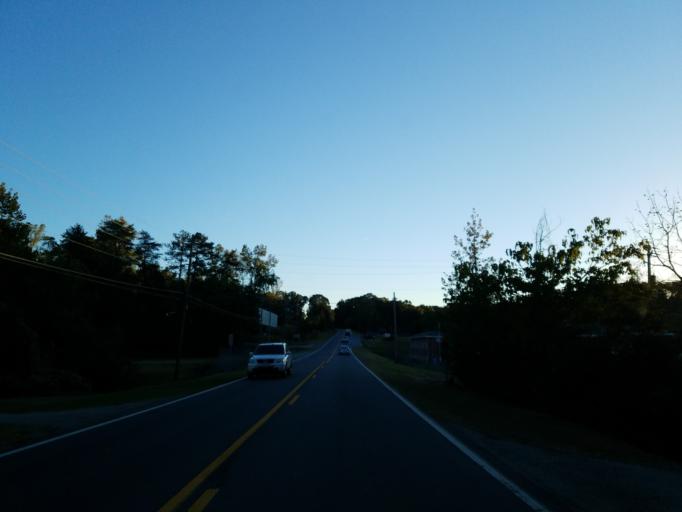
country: US
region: Georgia
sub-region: Forsyth County
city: Cumming
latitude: 34.2290
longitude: -84.1267
